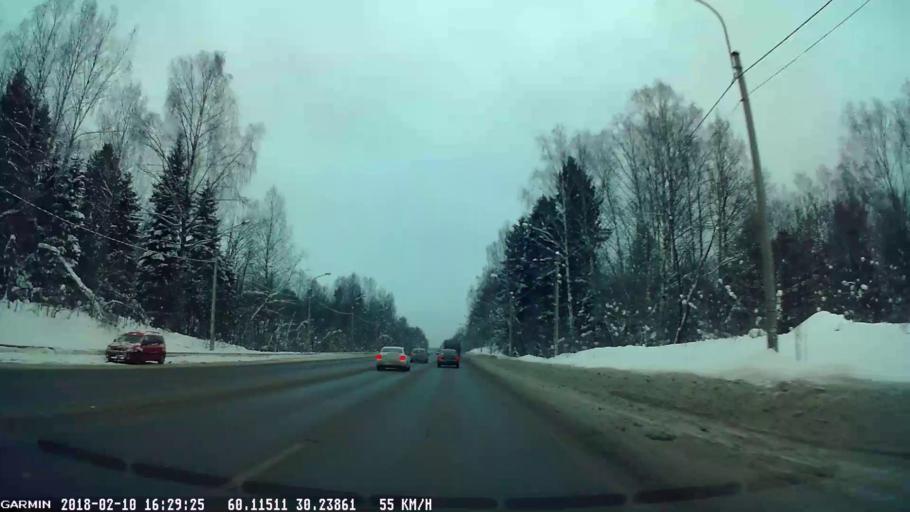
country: RU
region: St.-Petersburg
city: Levashovo
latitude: 60.1155
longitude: 30.2382
